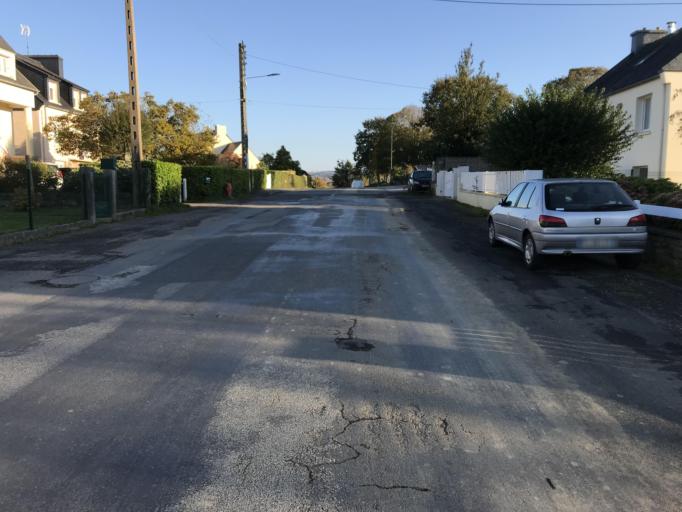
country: FR
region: Brittany
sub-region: Departement du Finistere
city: Le Faou
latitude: 48.2980
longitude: -4.1908
